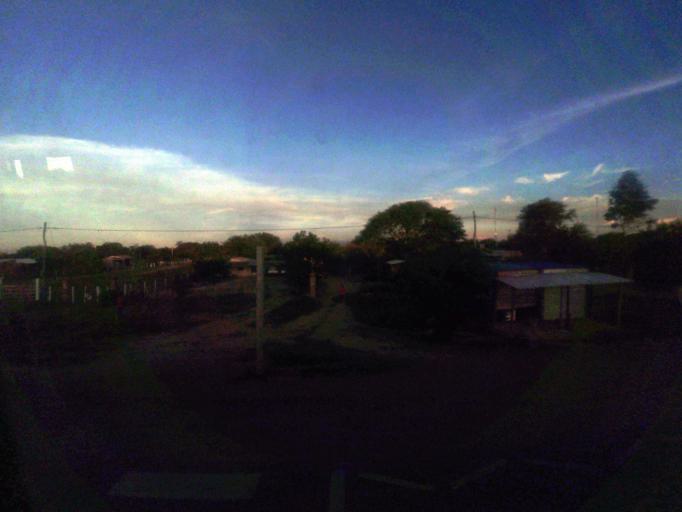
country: BO
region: Santa Cruz
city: Jorochito
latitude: -18.4522
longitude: -63.2114
